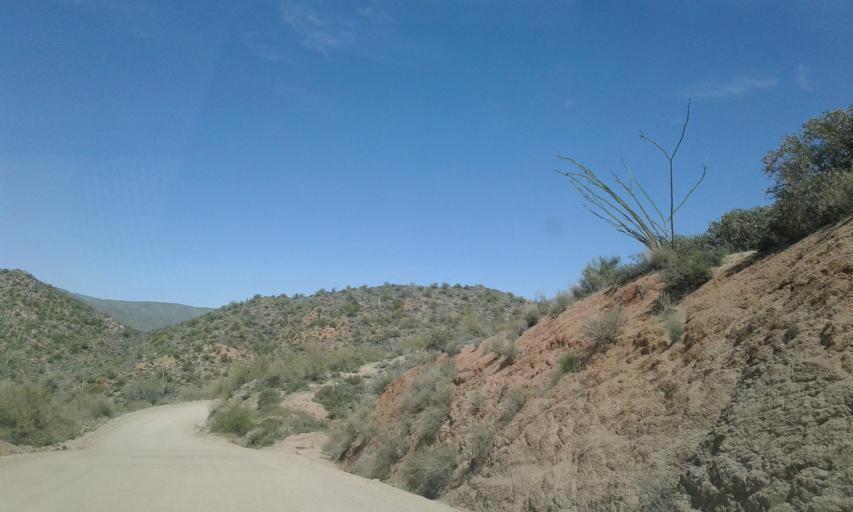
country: US
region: Arizona
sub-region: Gila County
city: Tonto Basin
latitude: 33.5895
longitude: -111.2103
